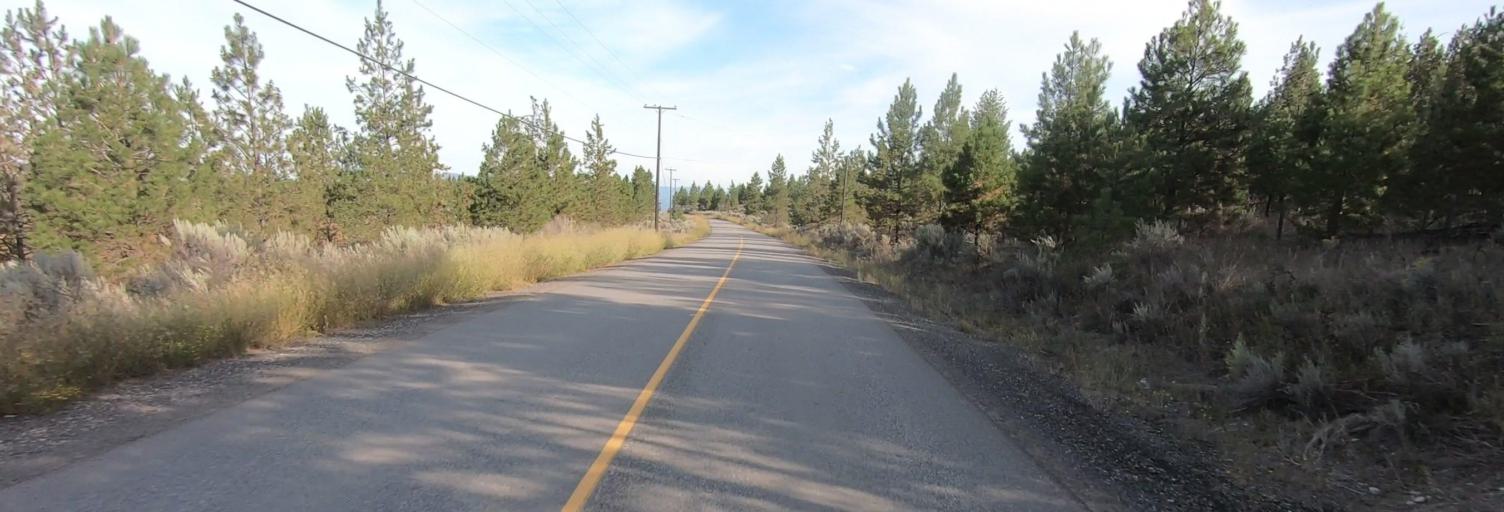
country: CA
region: British Columbia
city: Kamloops
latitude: 50.6456
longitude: -120.4506
